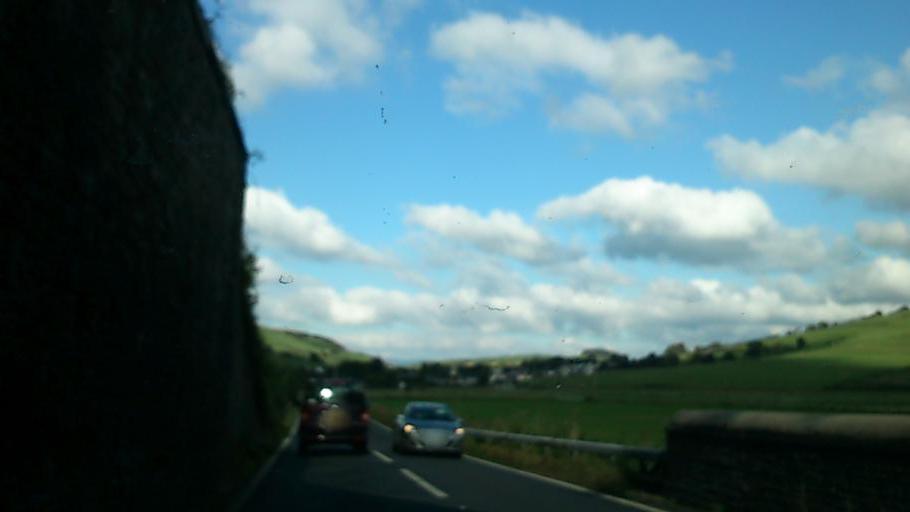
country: GB
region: Wales
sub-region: County of Ceredigion
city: Bow Street
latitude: 52.4342
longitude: -4.0323
